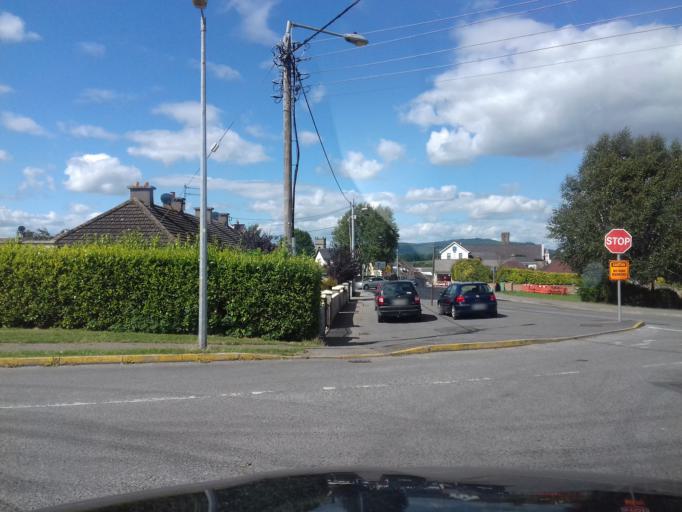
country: IE
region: Munster
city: Carrick-on-Suir
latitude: 52.3420
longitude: -7.4160
